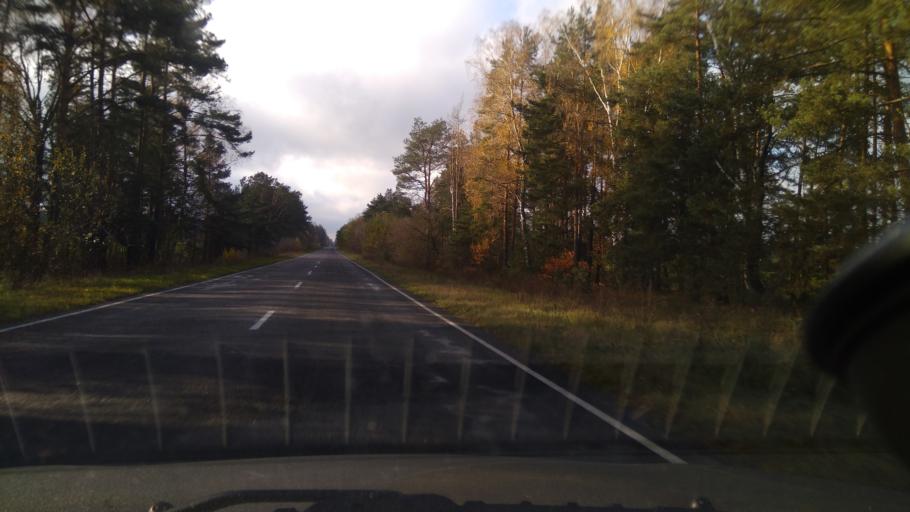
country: BY
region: Minsk
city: Urechcha
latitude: 53.2099
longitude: 27.9883
